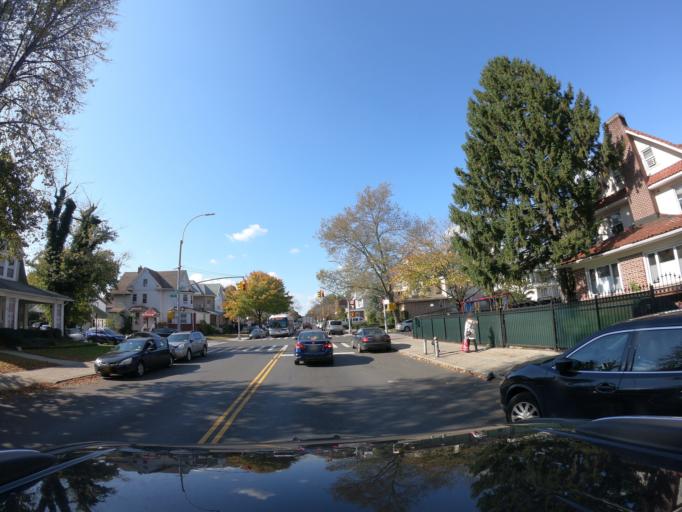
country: US
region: New York
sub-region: Kings County
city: Brooklyn
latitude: 40.6257
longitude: -73.9572
